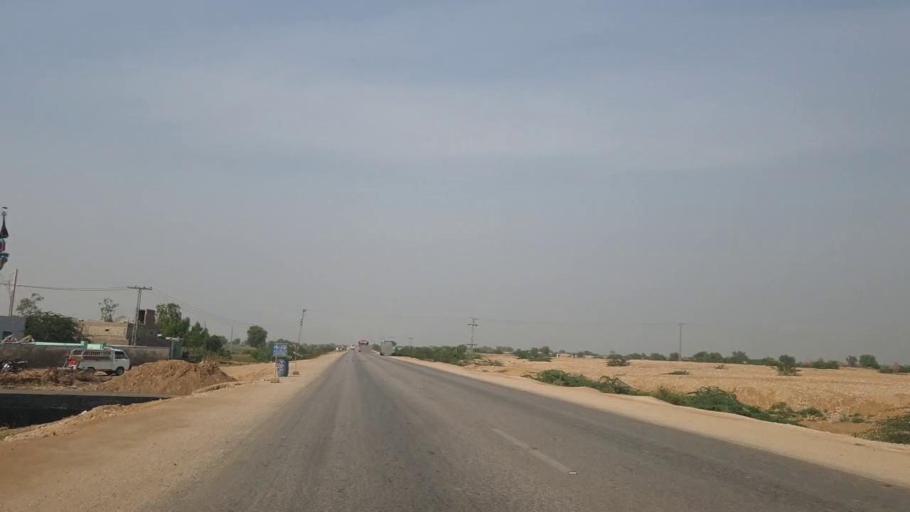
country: PK
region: Sindh
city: Sann
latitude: 26.0612
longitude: 68.1035
